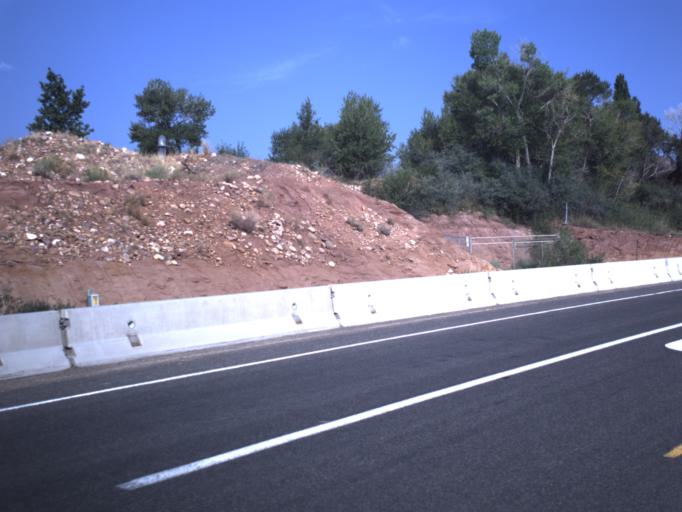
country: US
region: Utah
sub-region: Duchesne County
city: Duchesne
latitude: 40.2977
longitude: -110.2365
